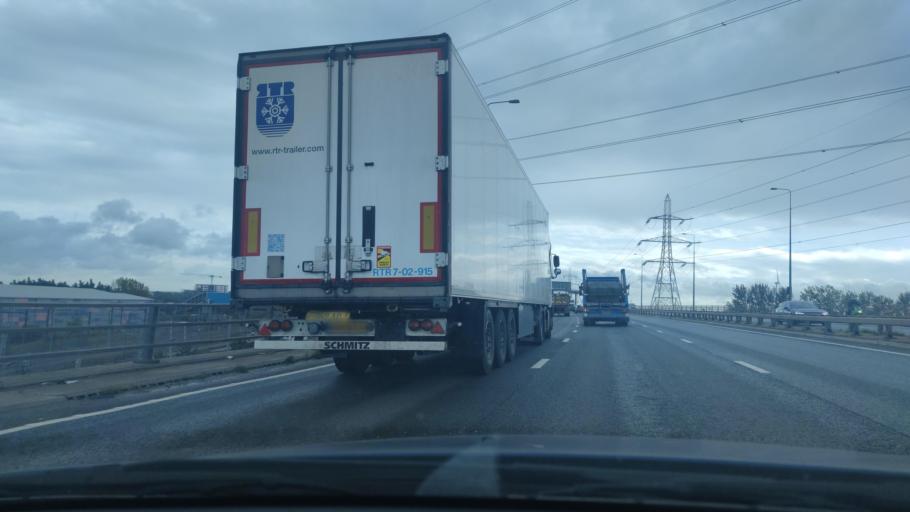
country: GB
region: England
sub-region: Greater London
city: Dagenham
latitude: 51.5252
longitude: 0.1470
